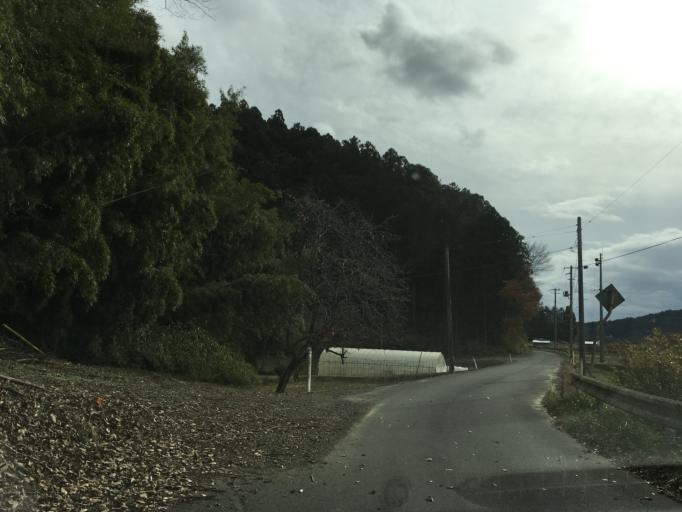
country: JP
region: Iwate
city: Ichinoseki
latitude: 38.7839
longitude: 141.2657
